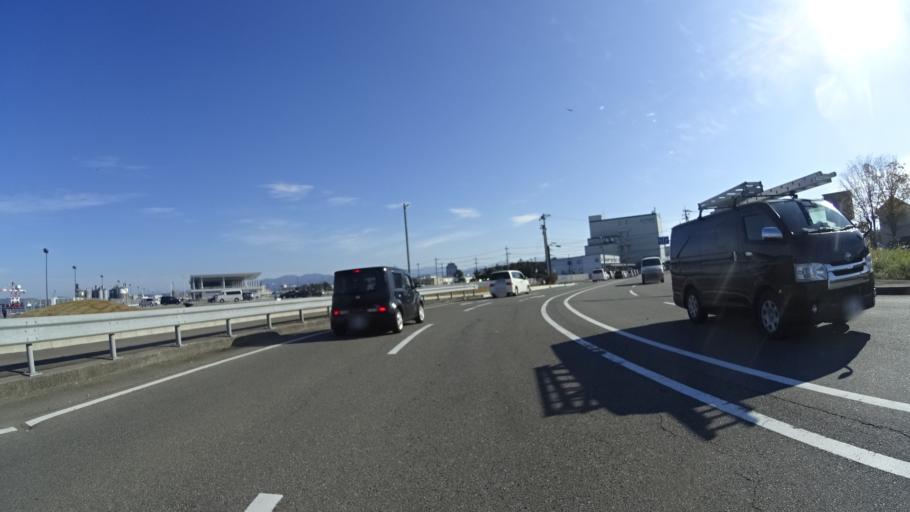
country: JP
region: Ishikawa
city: Kanazawa-shi
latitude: 36.6090
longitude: 136.6111
